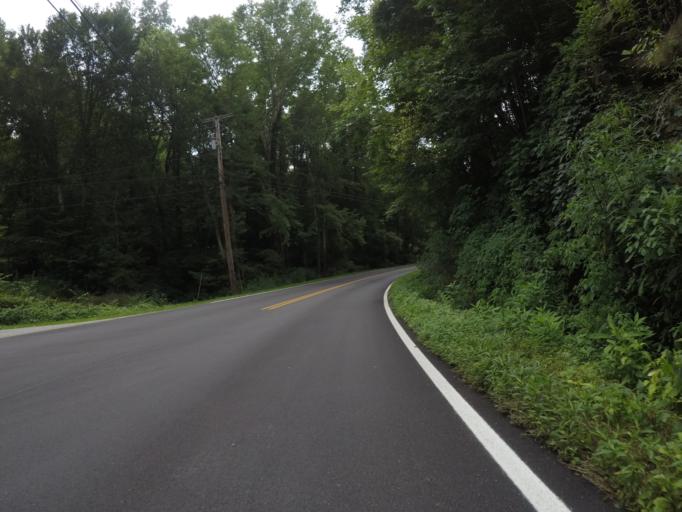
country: US
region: Kentucky
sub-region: Boyd County
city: Catlettsburg
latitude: 38.4360
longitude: -82.6274
